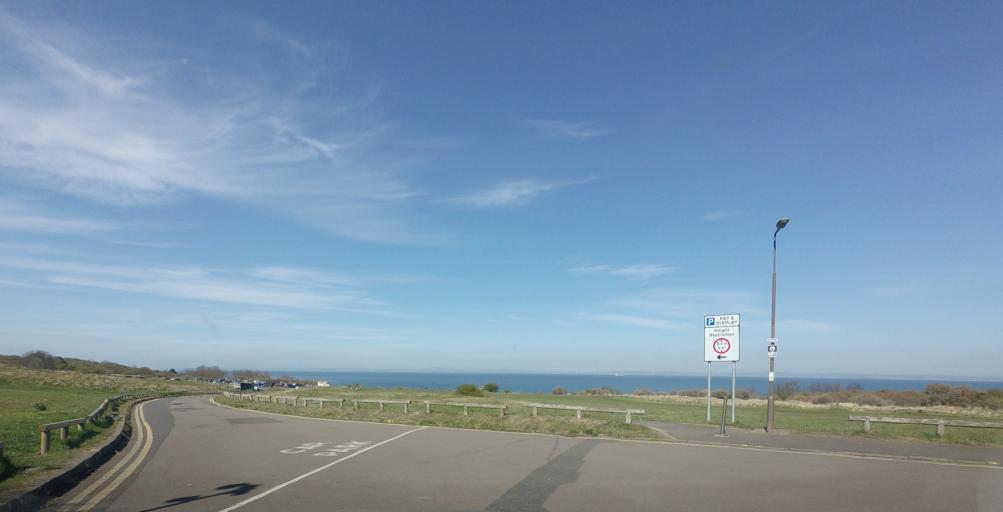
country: GB
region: Scotland
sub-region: East Lothian
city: Gullane
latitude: 56.0376
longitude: -2.8377
